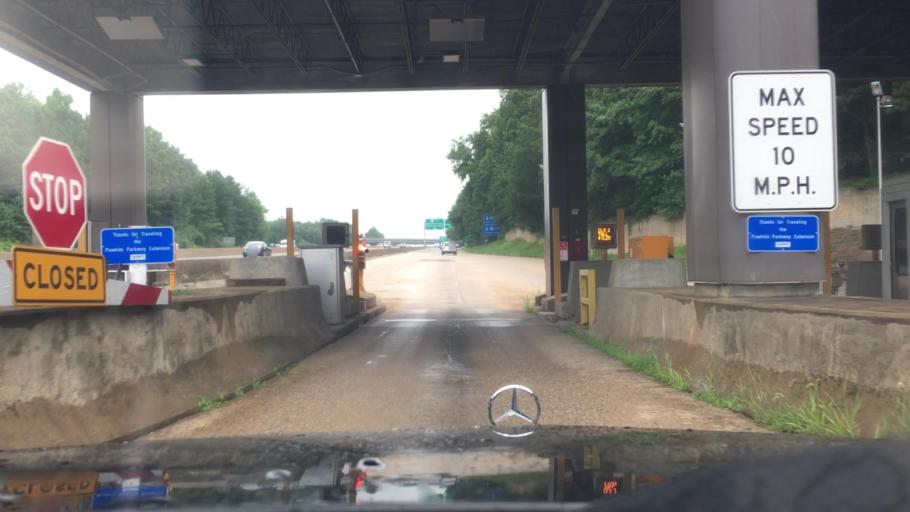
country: US
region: Virginia
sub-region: Chesterfield County
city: Bon Air
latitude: 37.5008
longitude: -77.5581
